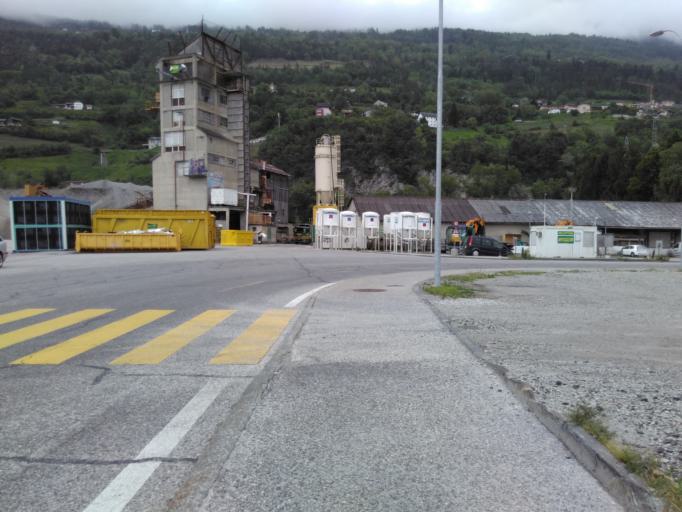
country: CH
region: Valais
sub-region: Sion District
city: Sitten
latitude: 46.2228
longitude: 7.3600
